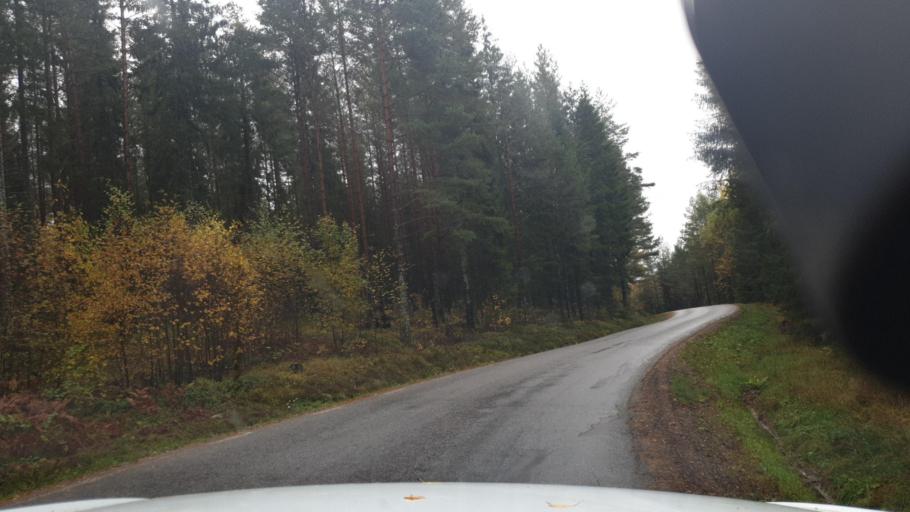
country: SE
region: Vaermland
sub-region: Karlstads Kommun
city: Valberg
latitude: 59.4165
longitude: 13.1521
